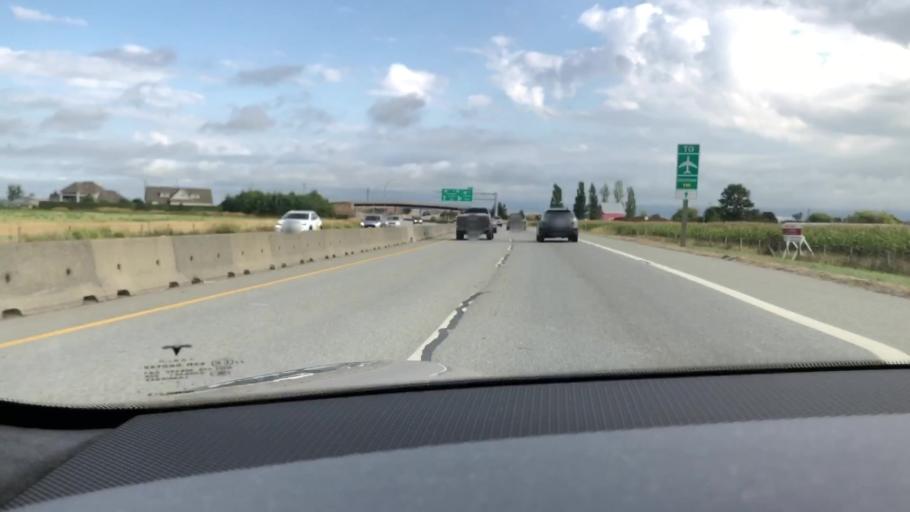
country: CA
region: British Columbia
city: Ladner
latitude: 49.0505
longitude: -123.0578
